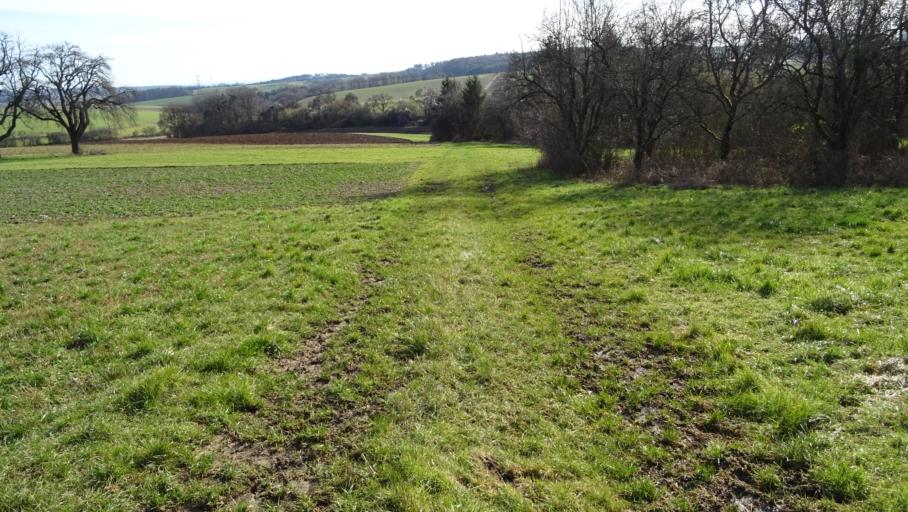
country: DE
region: Baden-Wuerttemberg
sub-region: Karlsruhe Region
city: Mosbach
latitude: 49.3668
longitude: 9.1917
